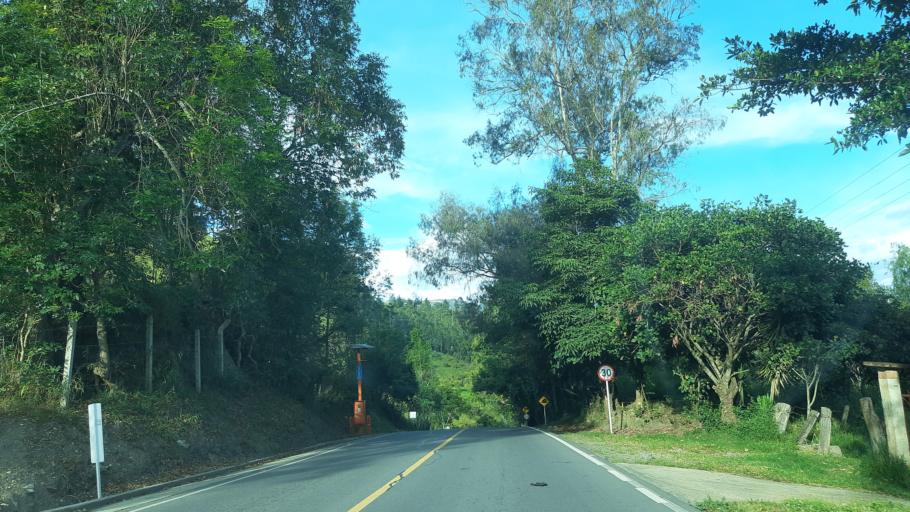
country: CO
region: Cundinamarca
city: Macheta
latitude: 5.0780
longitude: -73.5970
